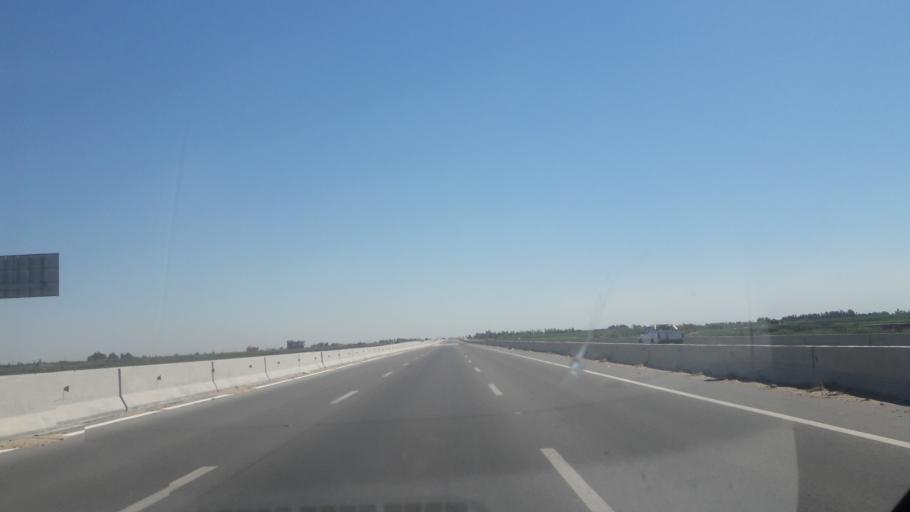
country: EG
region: Al Isma'iliyah
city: Ismailia
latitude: 30.8948
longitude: 32.1780
